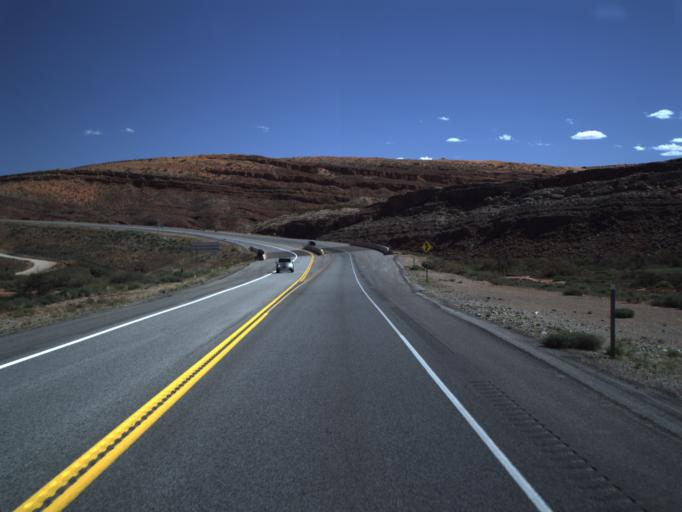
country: US
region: Utah
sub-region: Washington County
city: Washington
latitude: 37.1129
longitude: -113.4406
